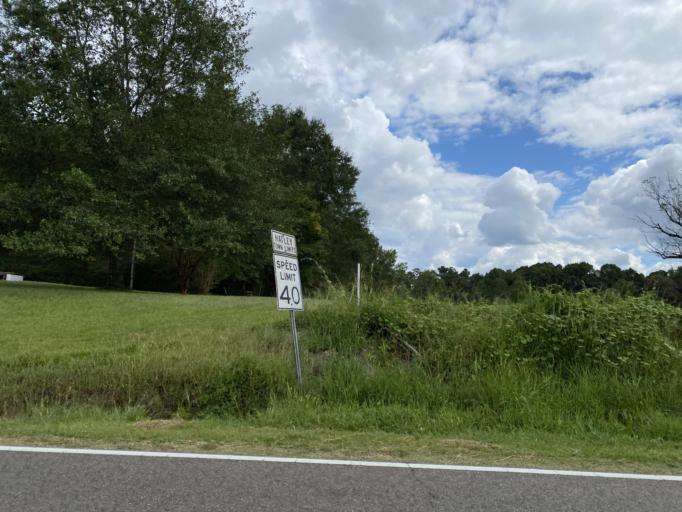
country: US
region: Mississippi
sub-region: Monroe County
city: Amory
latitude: 33.9747
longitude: -88.4407
